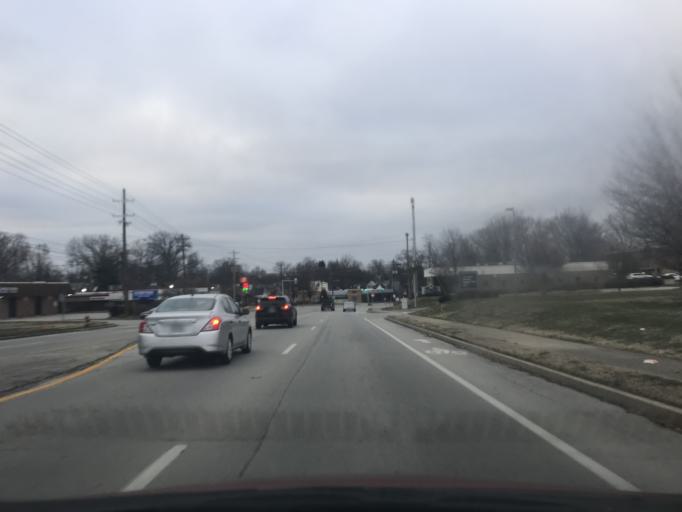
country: US
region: Kentucky
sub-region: Jefferson County
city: Audubon Park
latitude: 38.2188
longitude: -85.7278
